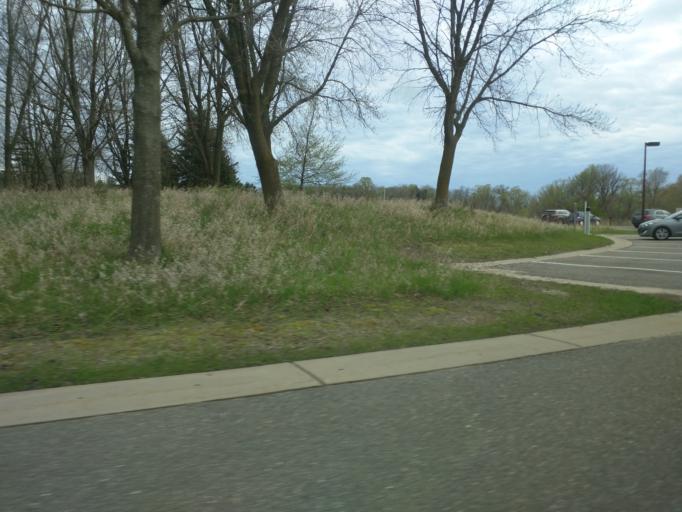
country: US
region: Minnesota
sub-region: Washington County
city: Cottage Grove
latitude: 44.7662
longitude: -92.9356
